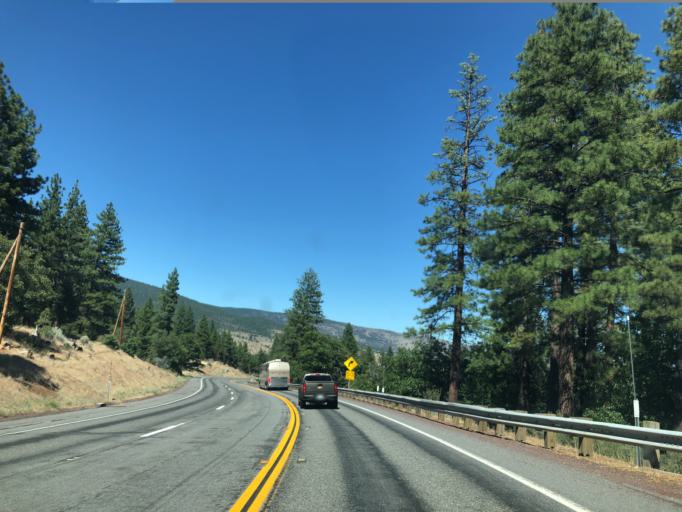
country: US
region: California
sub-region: Lassen County
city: Susanville
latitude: 40.4230
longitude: -120.6839
